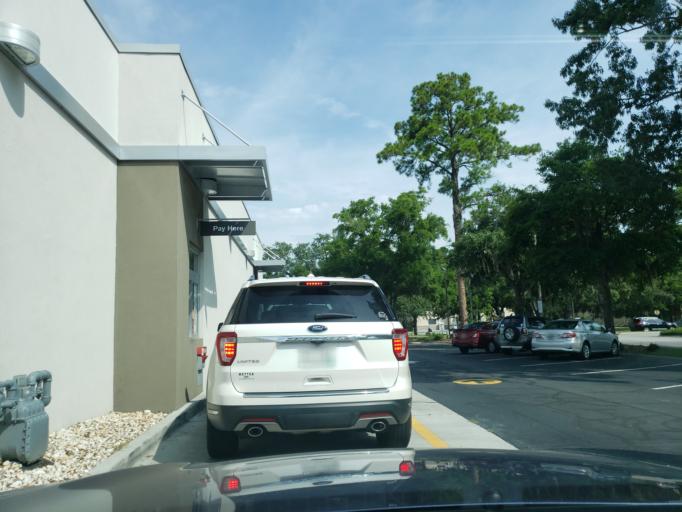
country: US
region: Georgia
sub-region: Chatham County
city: Wilmington Island
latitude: 32.0159
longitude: -80.9781
